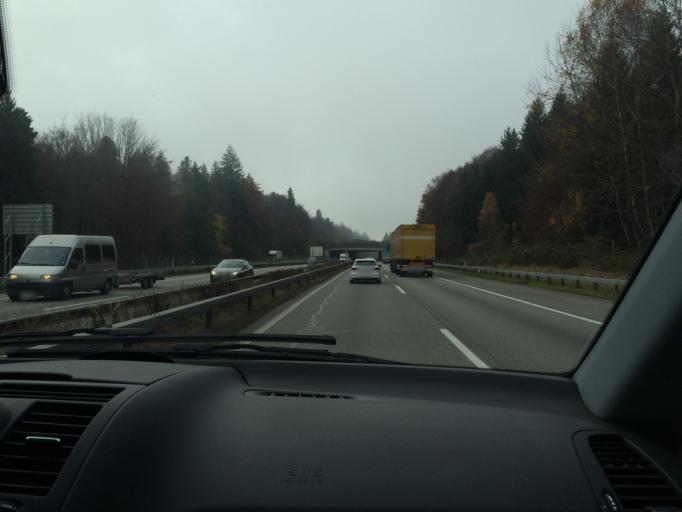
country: CH
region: Bern
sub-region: Emmental District
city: Lyssach
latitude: 47.0650
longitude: 7.5612
